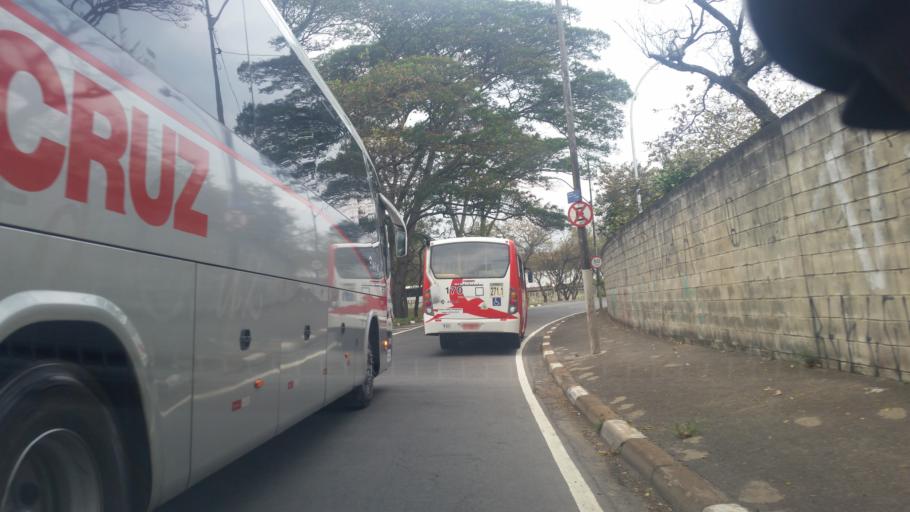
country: BR
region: Sao Paulo
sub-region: Campinas
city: Campinas
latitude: -22.9031
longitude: -47.0777
